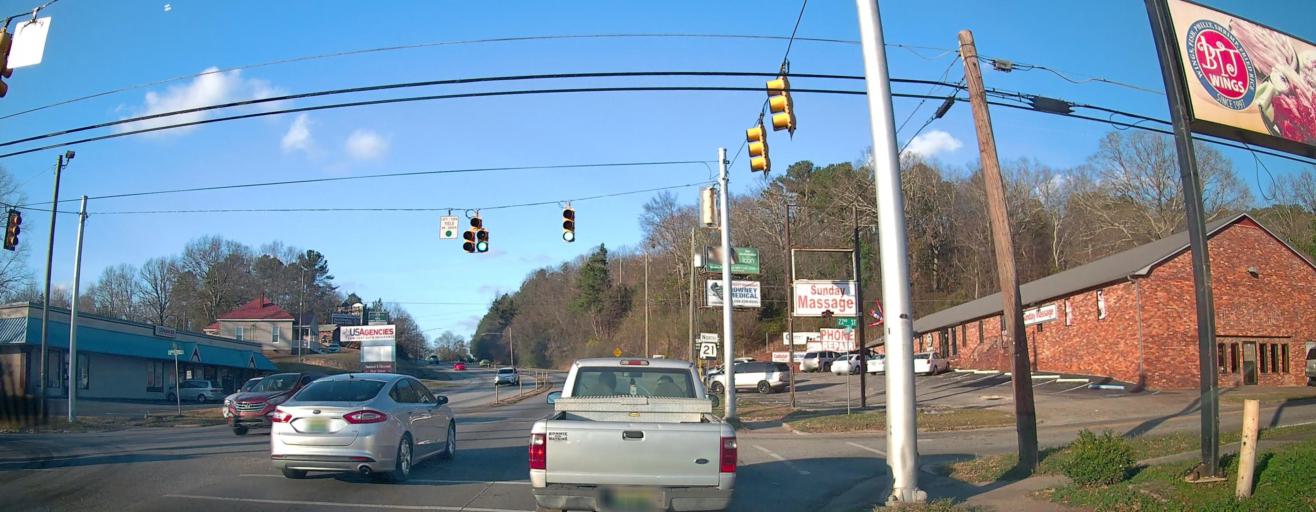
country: US
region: Alabama
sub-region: Calhoun County
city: Anniston
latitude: 33.6729
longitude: -85.8267
